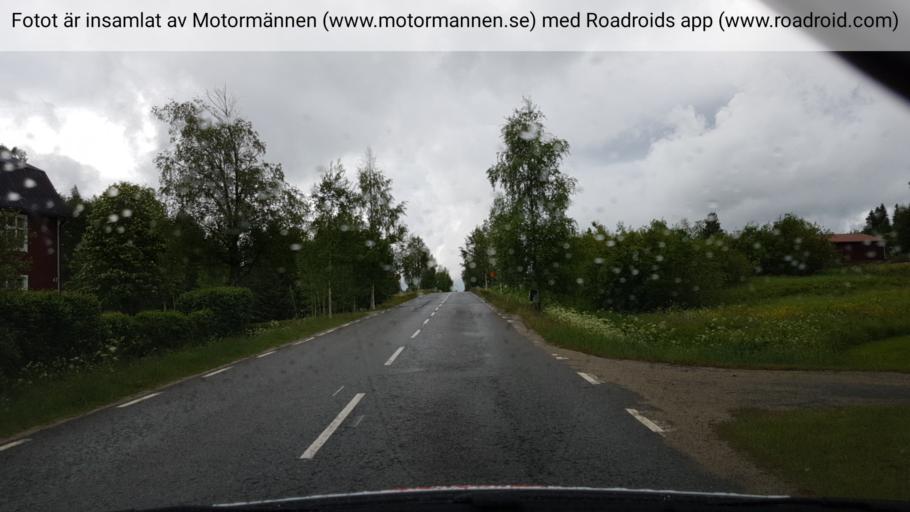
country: SE
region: Vaesterbotten
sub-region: Vannas Kommun
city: Vannasby
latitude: 63.8760
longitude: 19.8933
